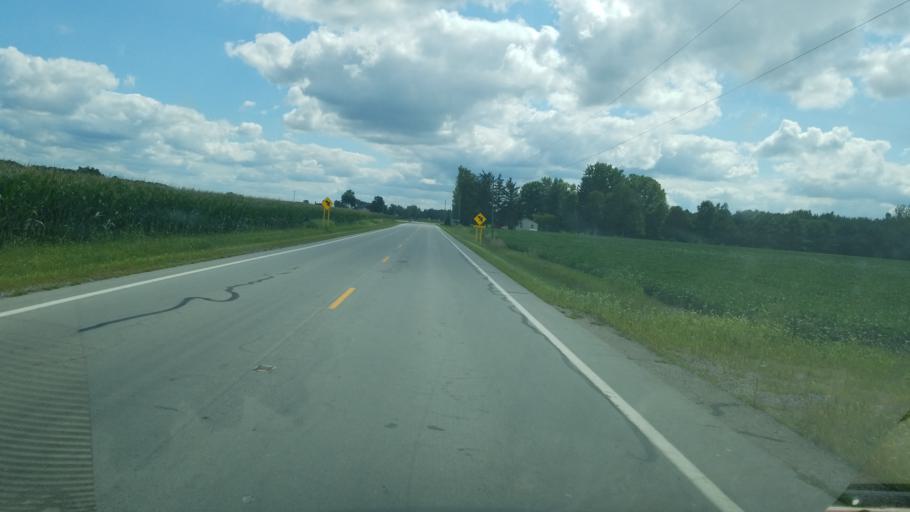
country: US
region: Ohio
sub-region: Allen County
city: Elida
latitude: 40.8359
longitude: -84.1380
